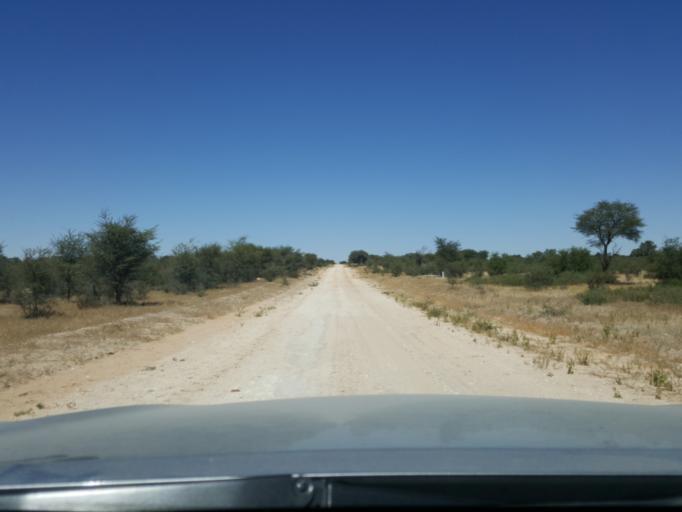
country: BW
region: Kgalagadi
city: Hukuntsi
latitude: -24.0132
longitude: 21.2145
